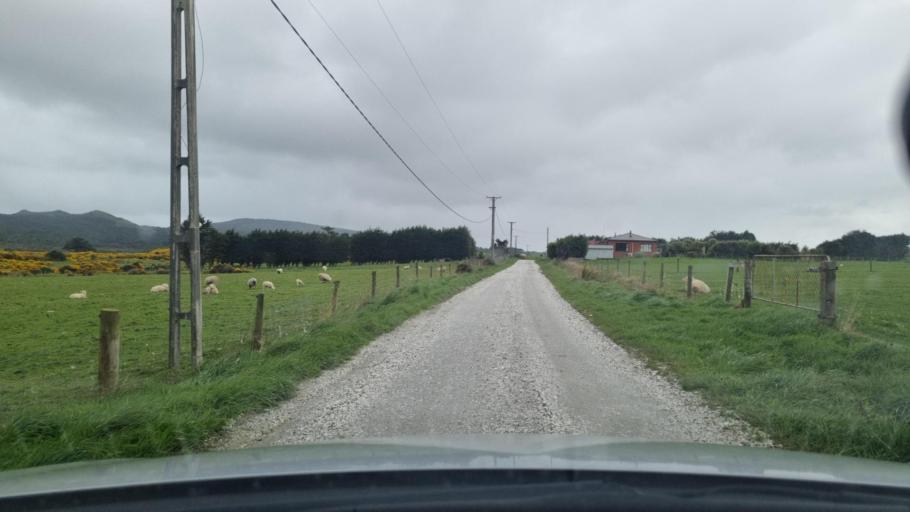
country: NZ
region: Southland
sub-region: Invercargill City
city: Bluff
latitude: -46.5425
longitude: 168.2939
